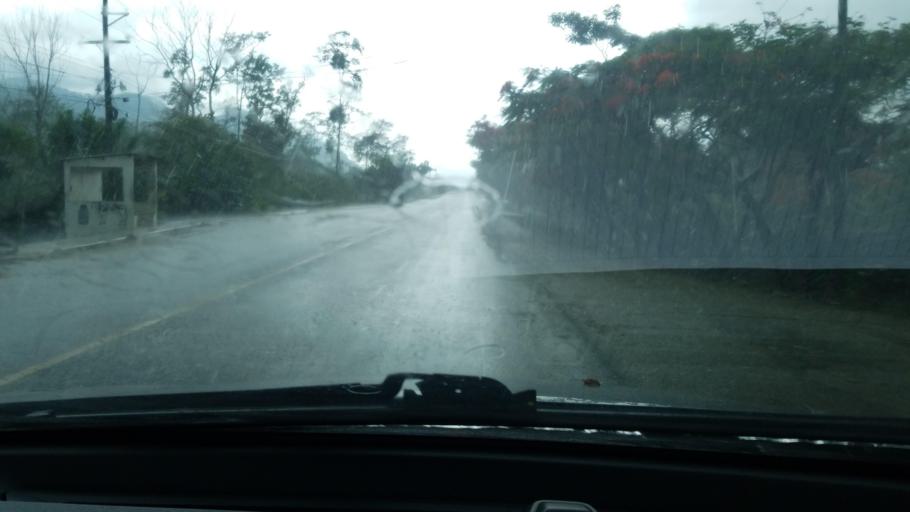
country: HN
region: Cortes
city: Rio Chiquito
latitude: 15.6296
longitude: -88.2514
